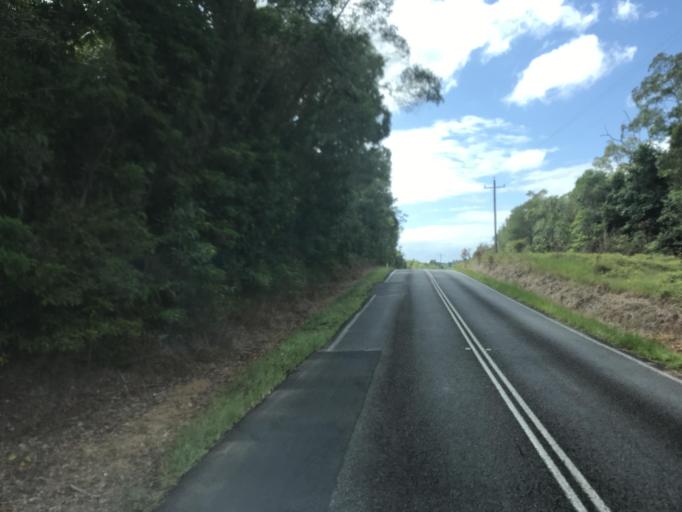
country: AU
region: Queensland
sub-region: Cassowary Coast
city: Innisfail
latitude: -17.8423
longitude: 146.0549
